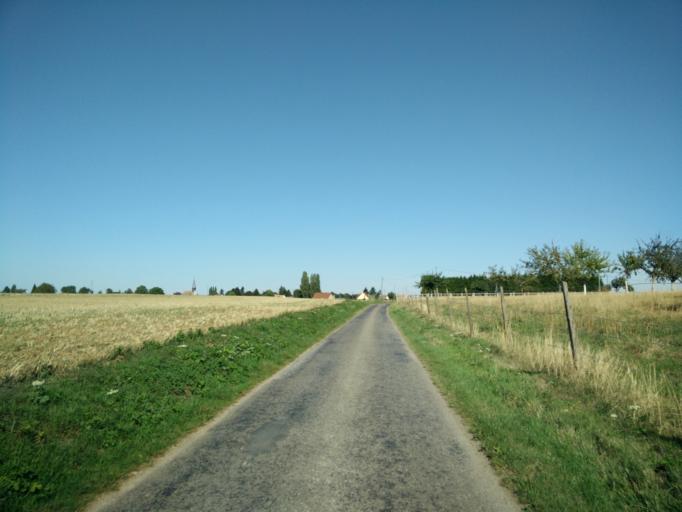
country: FR
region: Haute-Normandie
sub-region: Departement de l'Eure
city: Saint-Pierre-des-Fleurs
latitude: 49.1780
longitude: 0.9872
